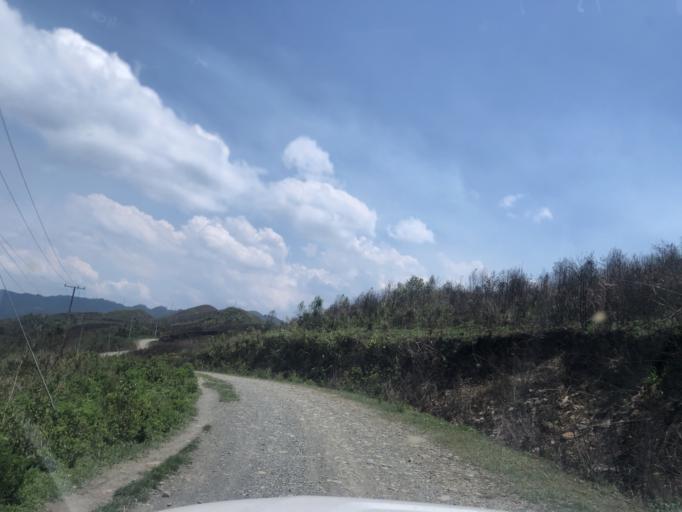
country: LA
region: Phongsali
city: Phongsali
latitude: 21.4186
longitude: 102.1843
